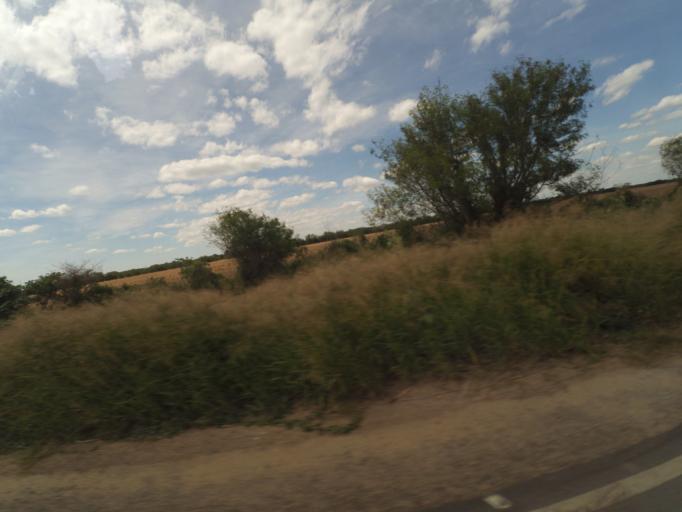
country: BO
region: Santa Cruz
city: Pailon
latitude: -17.5856
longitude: -62.0498
